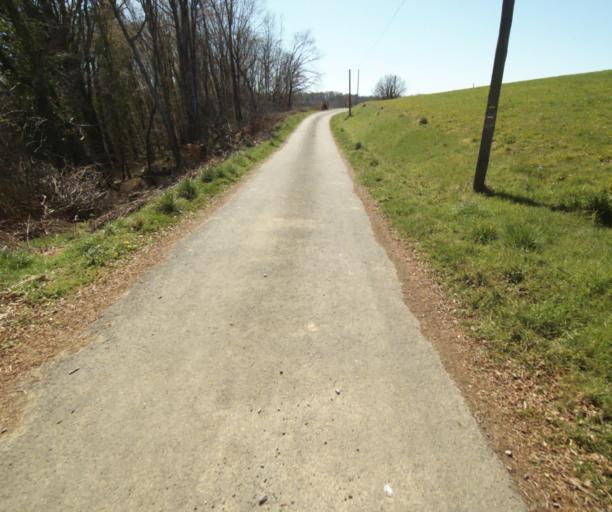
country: FR
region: Limousin
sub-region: Departement de la Correze
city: Chamboulive
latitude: 45.4312
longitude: 1.6840
